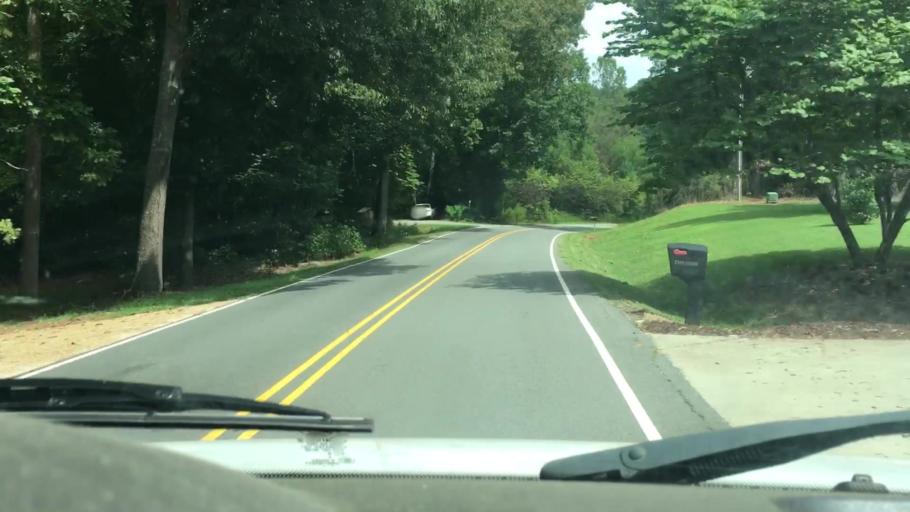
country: US
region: North Carolina
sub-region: Gaston County
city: Davidson
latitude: 35.5038
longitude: -80.8121
